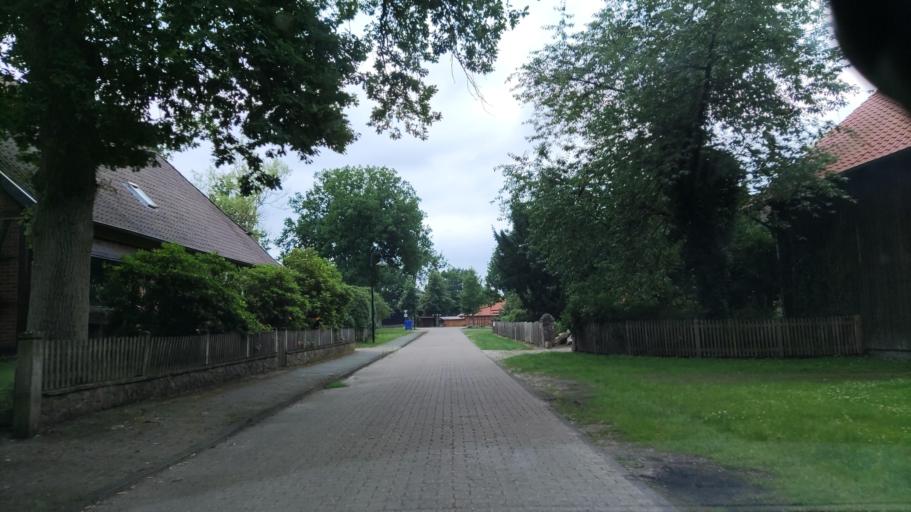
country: DE
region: Lower Saxony
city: Bad Fallingbostel
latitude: 52.8031
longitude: 9.6652
